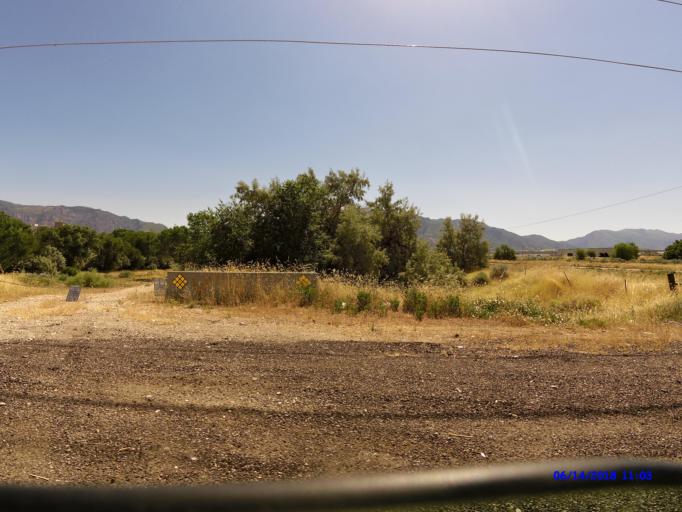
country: US
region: Utah
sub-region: Weber County
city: Riverdale
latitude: 41.2098
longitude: -112.0065
